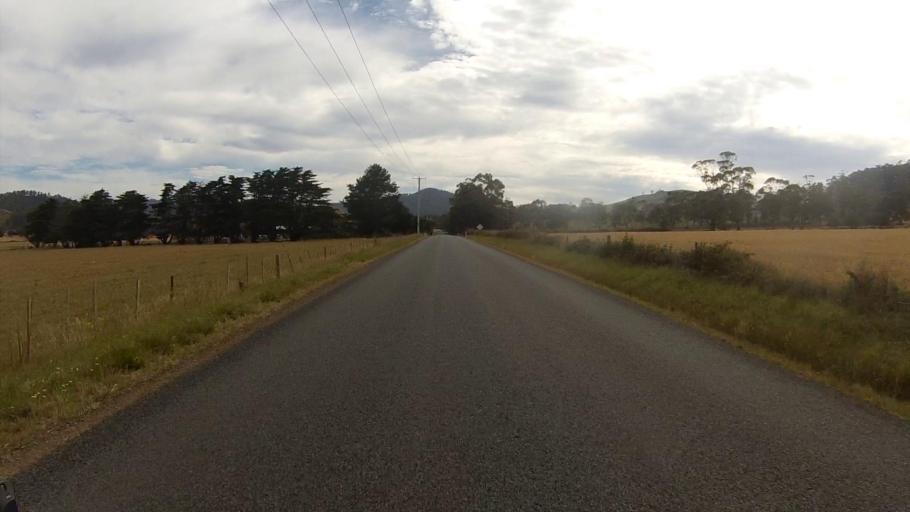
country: AU
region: Tasmania
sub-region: Sorell
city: Sorell
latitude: -42.7945
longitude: 147.7958
